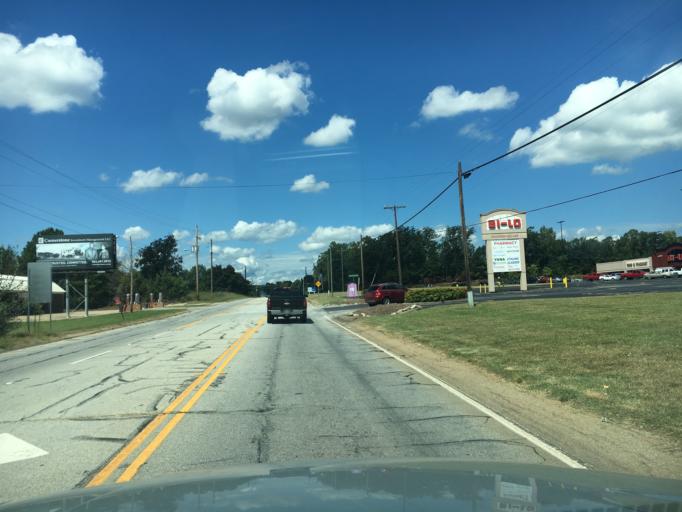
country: US
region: South Carolina
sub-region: Laurens County
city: Laurens
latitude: 34.4995
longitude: -82.0480
